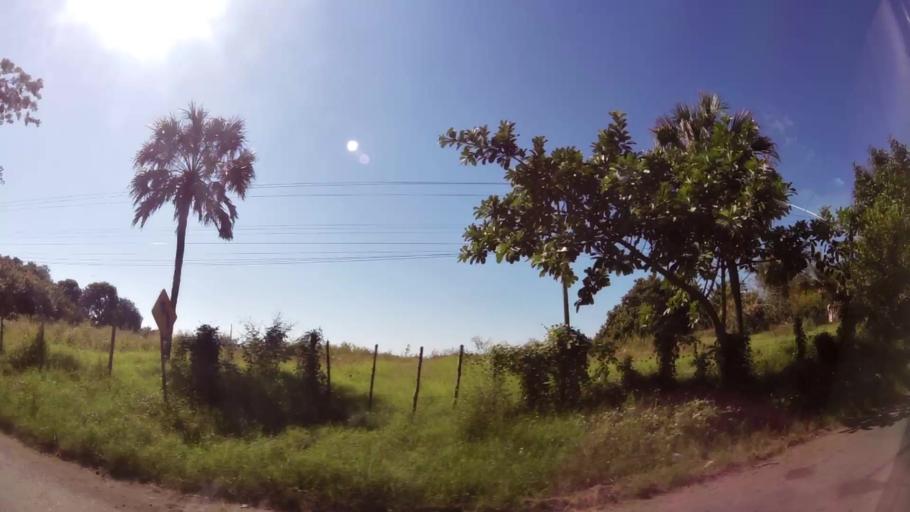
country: GT
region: Escuintla
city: Iztapa
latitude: 13.9144
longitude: -90.5443
